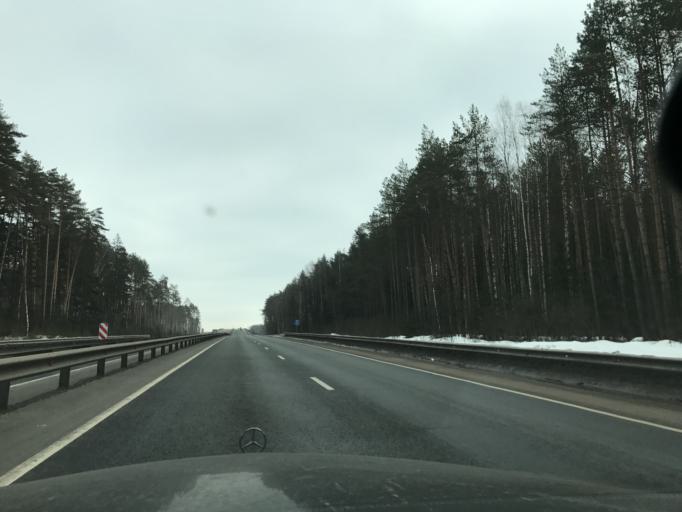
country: RU
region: Vladimir
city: Luknovo
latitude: 56.2369
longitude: 41.9616
